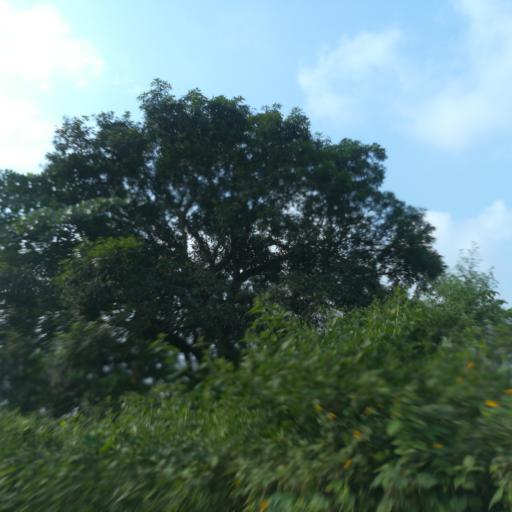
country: NG
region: Rivers
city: Okrika
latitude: 4.7822
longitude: 7.1441
